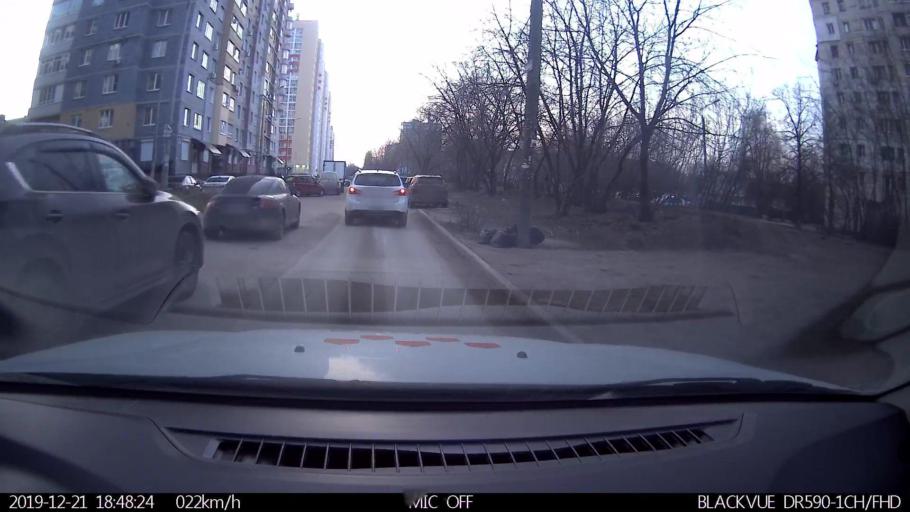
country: RU
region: Nizjnij Novgorod
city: Nizhniy Novgorod
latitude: 56.3260
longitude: 43.9294
